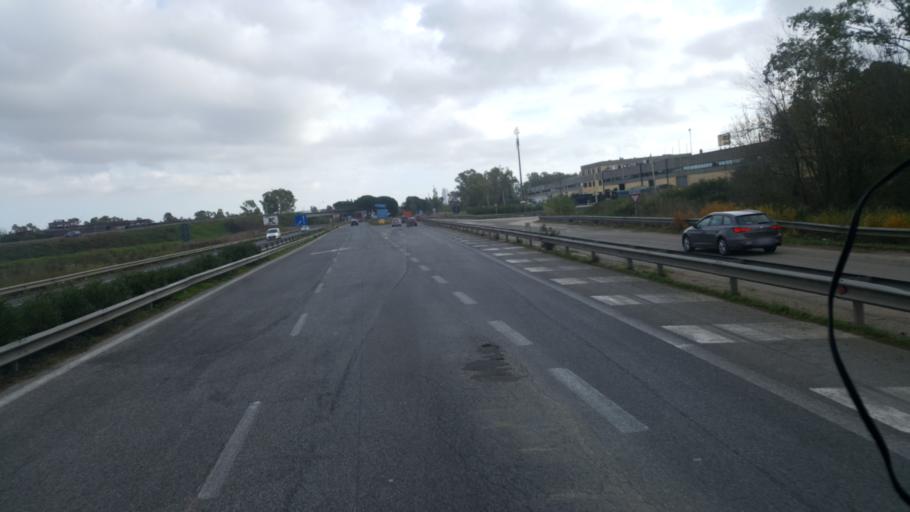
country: IT
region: Latium
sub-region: Provincia di Latina
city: Borgo Podgora
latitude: 41.4849
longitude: 12.8557
